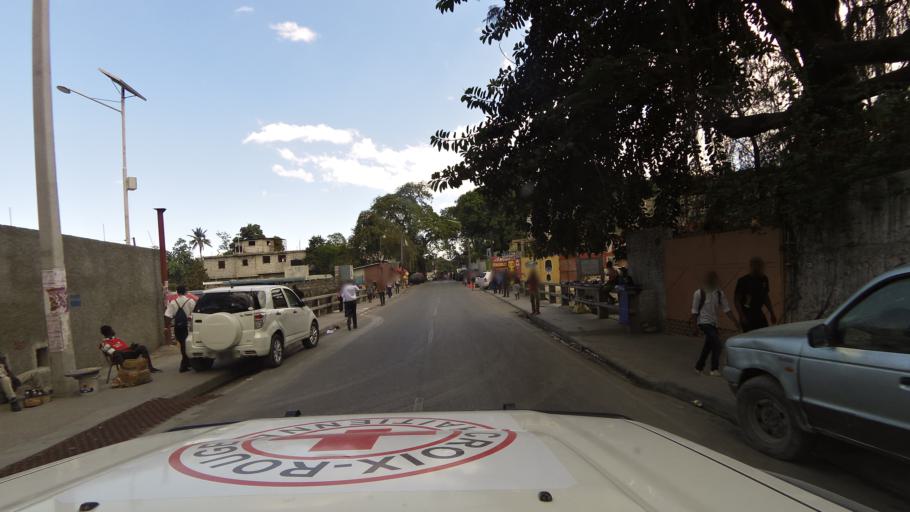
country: HT
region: Ouest
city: Petionville
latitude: 18.5133
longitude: -72.2843
